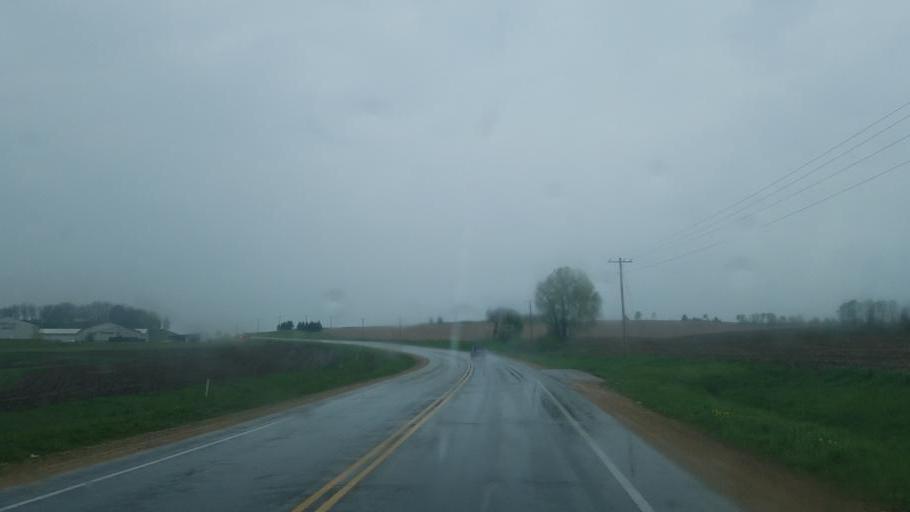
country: US
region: Wisconsin
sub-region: Sauk County
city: Reedsburg
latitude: 43.5651
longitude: -90.0845
